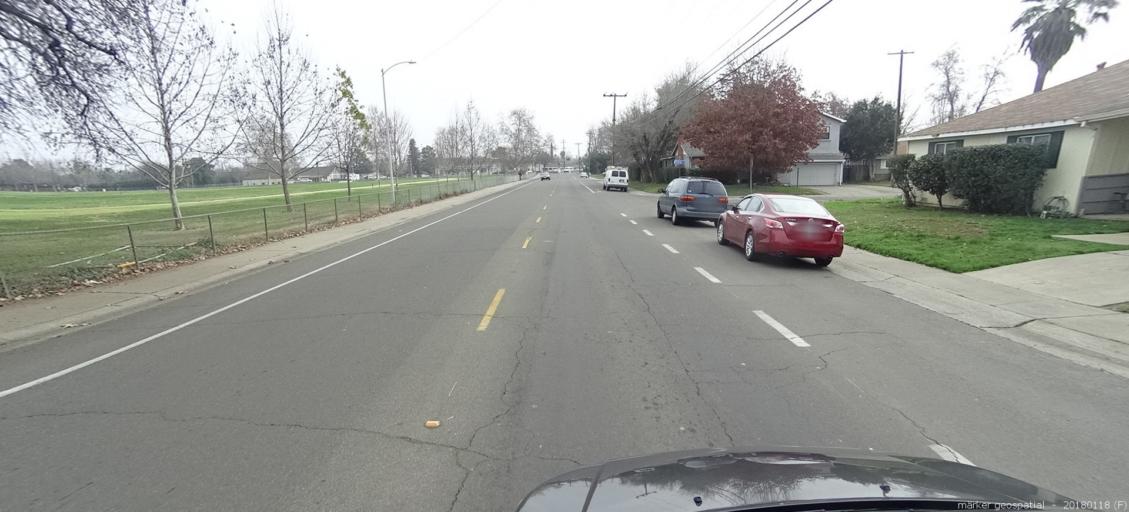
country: US
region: California
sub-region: Sacramento County
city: Rancho Cordova
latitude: 38.5977
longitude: -121.3069
